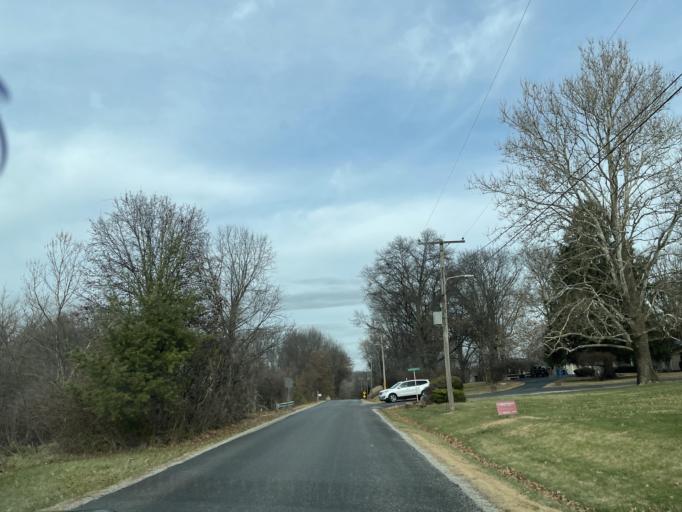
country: US
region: Illinois
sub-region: Sangamon County
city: Leland Grove
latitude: 39.8061
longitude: -89.7298
